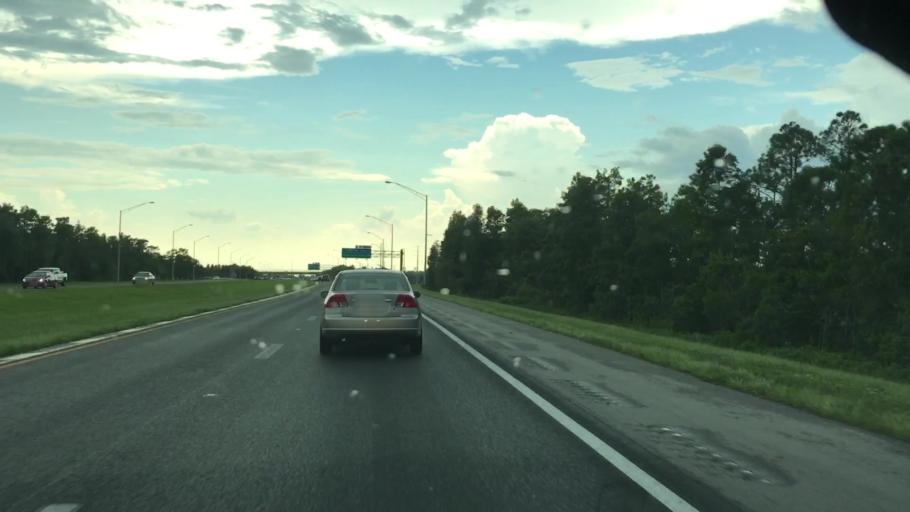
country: US
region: Florida
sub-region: Osceola County
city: Buenaventura Lakes
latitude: 28.3827
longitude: -81.2683
